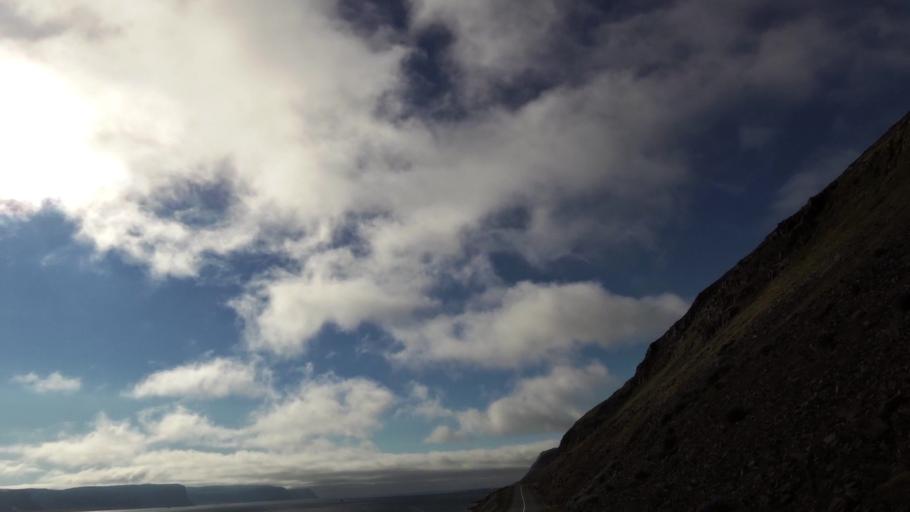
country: IS
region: West
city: Olafsvik
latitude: 65.5640
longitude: -23.9168
